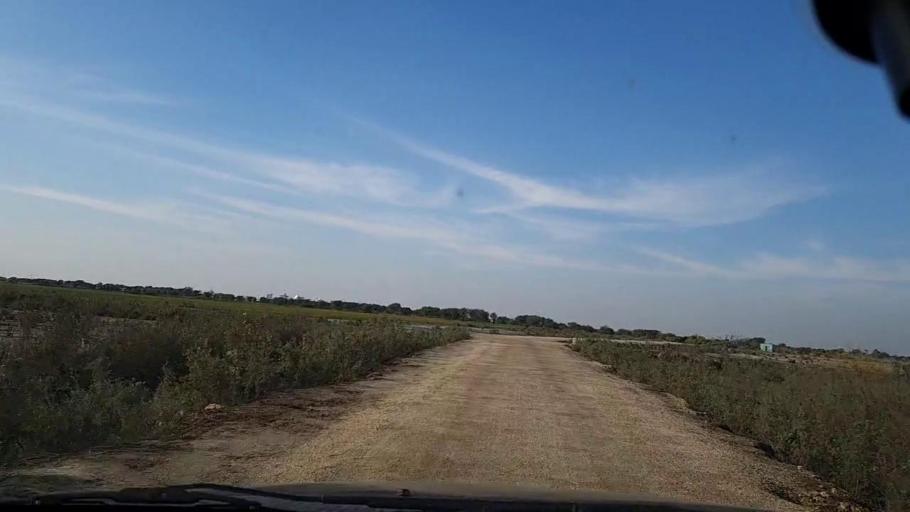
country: PK
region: Sindh
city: Mirpur Batoro
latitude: 24.6345
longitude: 68.2986
